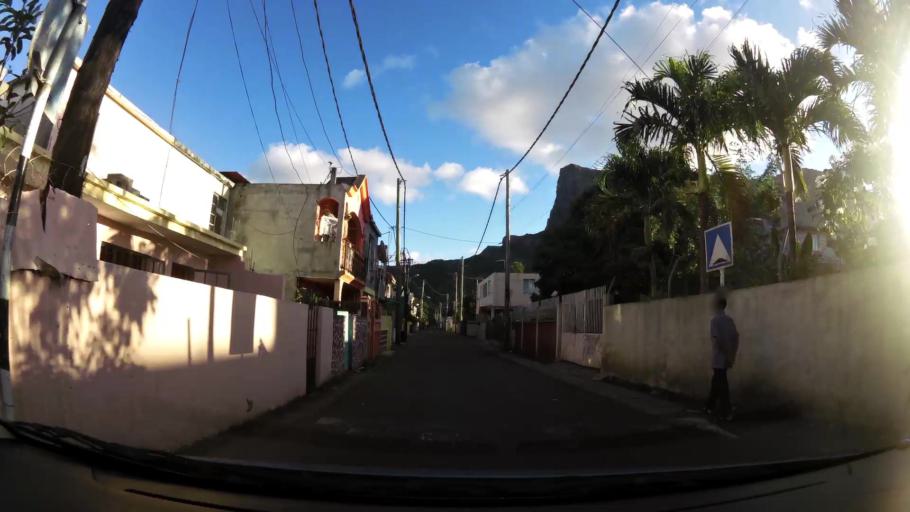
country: MU
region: Plaines Wilhems
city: Quatre Bornes
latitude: -20.2607
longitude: 57.4651
